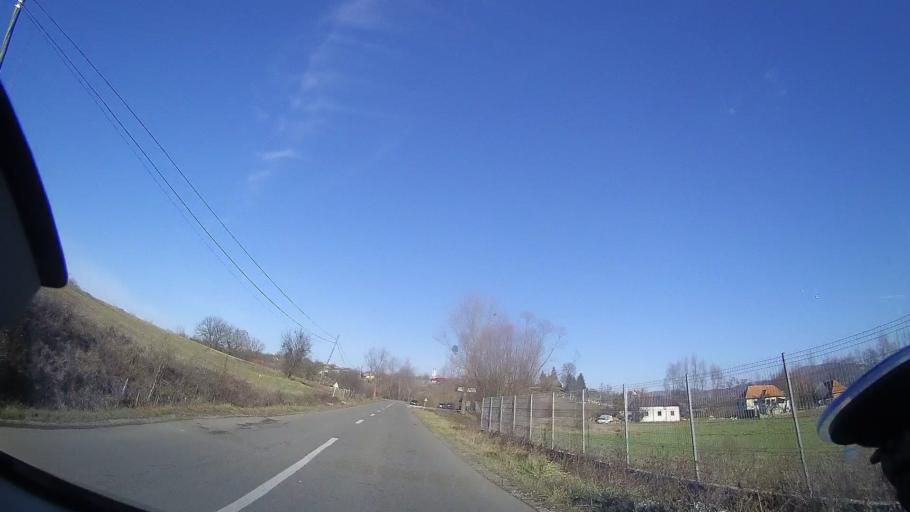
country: RO
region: Bihor
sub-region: Comuna Bratca
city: Beznea
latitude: 46.9507
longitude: 22.6121
